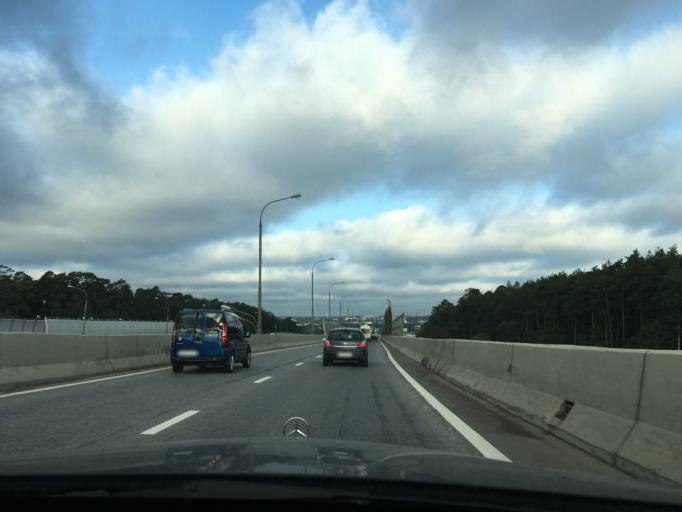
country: RU
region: Moscow
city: Rublevo
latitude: 55.7910
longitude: 37.3675
